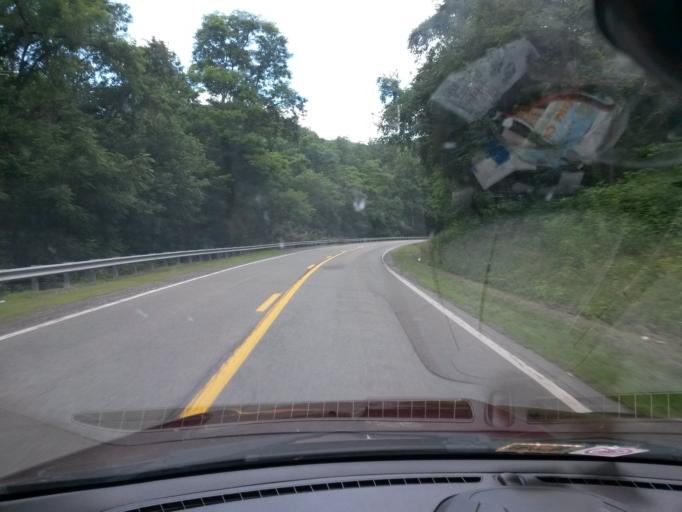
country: US
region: West Virginia
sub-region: Pendleton County
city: Franklin
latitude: 38.7089
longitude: -79.3042
